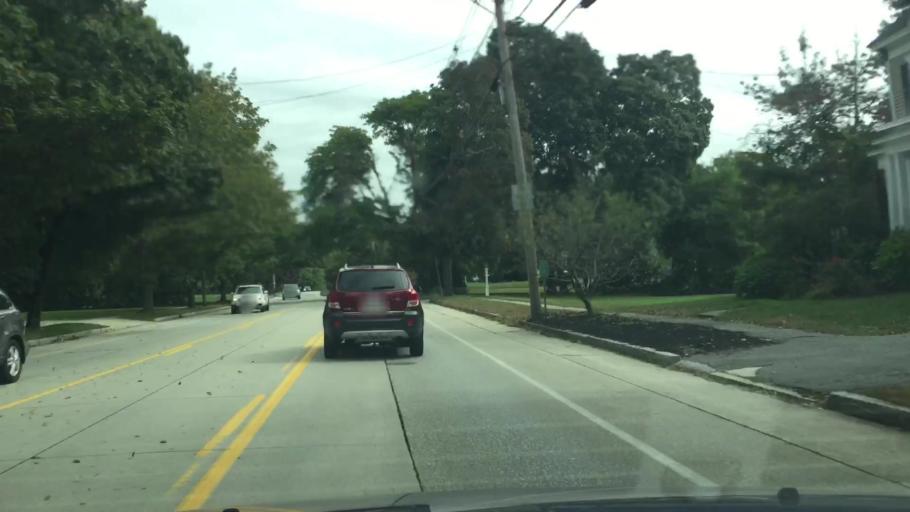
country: US
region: Massachusetts
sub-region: Middlesex County
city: Dracut
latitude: 42.6453
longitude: -71.2782
